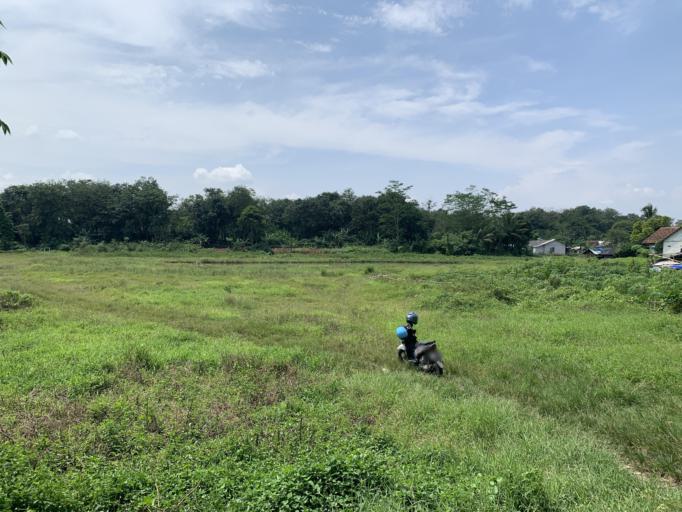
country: ID
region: West Java
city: Serpong
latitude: -6.3995
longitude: 106.6264
